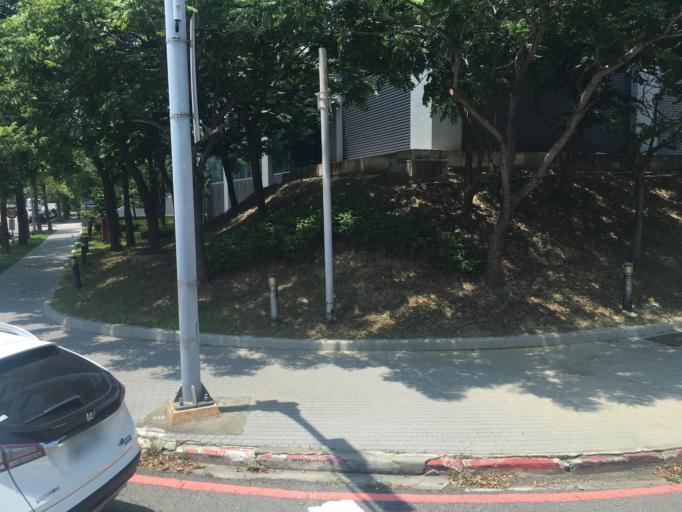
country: TW
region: Taiwan
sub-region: Hsinchu
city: Hsinchu
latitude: 24.7731
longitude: 121.0148
